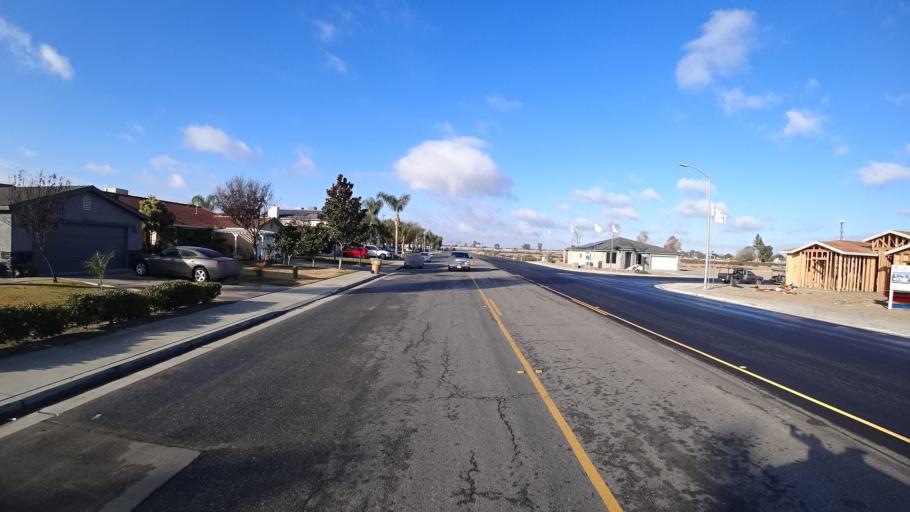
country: US
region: California
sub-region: Kern County
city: Greenfield
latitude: 35.2885
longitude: -119.0176
